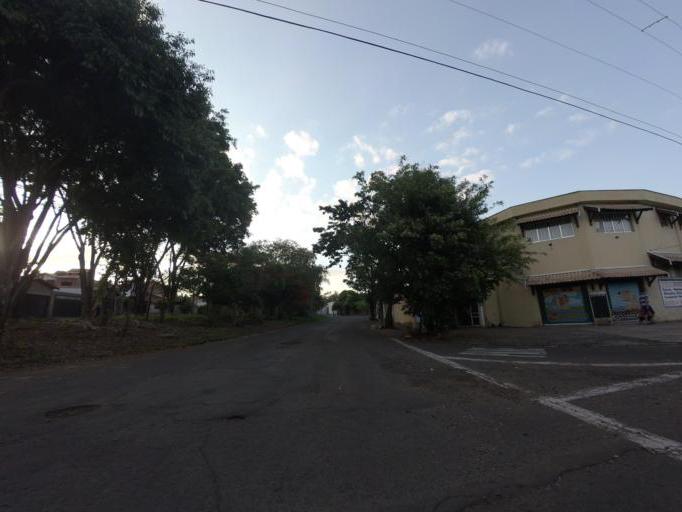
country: BR
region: Sao Paulo
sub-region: Piracicaba
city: Piracicaba
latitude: -22.7611
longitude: -47.6094
